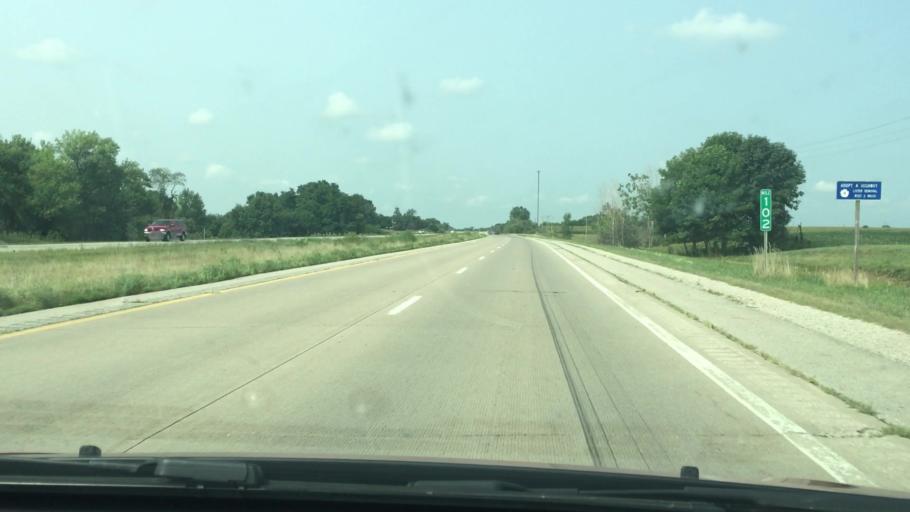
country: US
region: Iowa
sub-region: Cedar County
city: Durant
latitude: 41.5194
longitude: -90.8836
